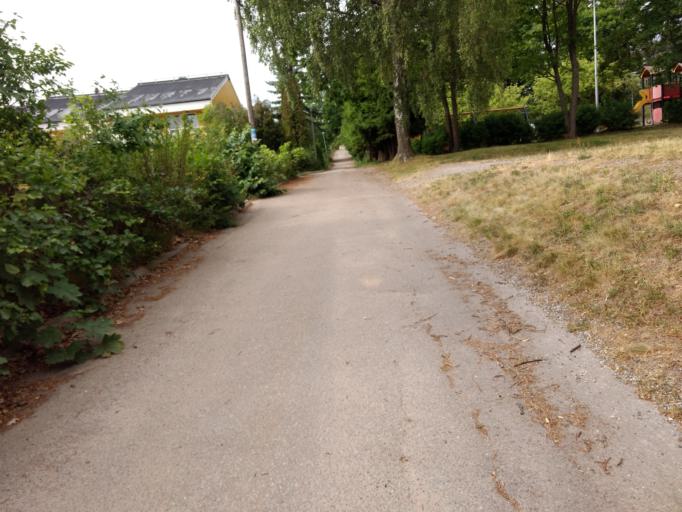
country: SE
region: Stockholm
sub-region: Upplands Vasby Kommun
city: Upplands Vaesby
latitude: 59.5240
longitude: 17.9079
